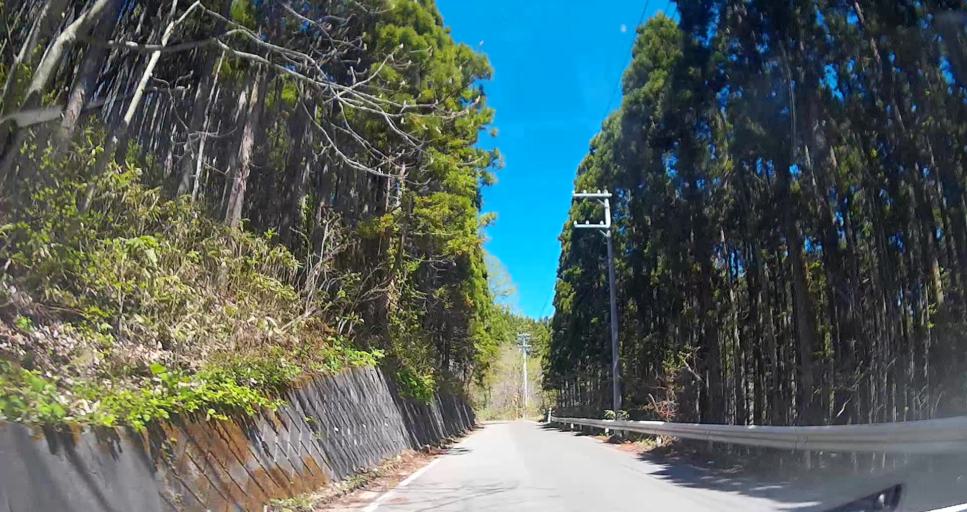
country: JP
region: Aomori
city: Mutsu
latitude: 41.1201
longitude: 141.3922
